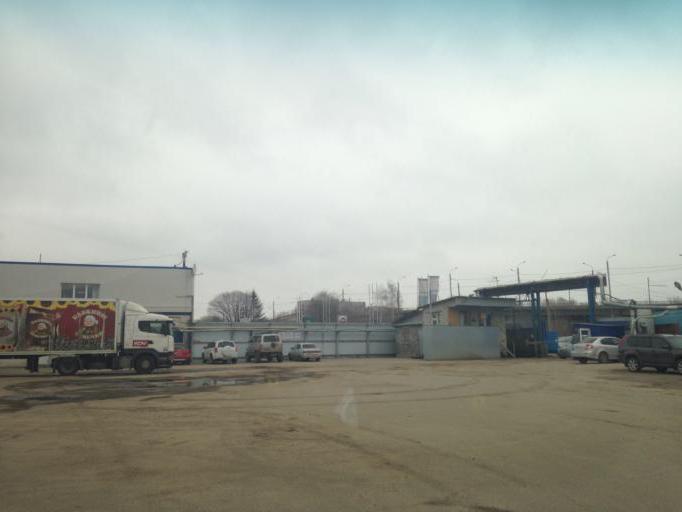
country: RU
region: Ulyanovsk
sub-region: Ulyanovskiy Rayon
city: Ulyanovsk
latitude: 54.3059
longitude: 48.3075
